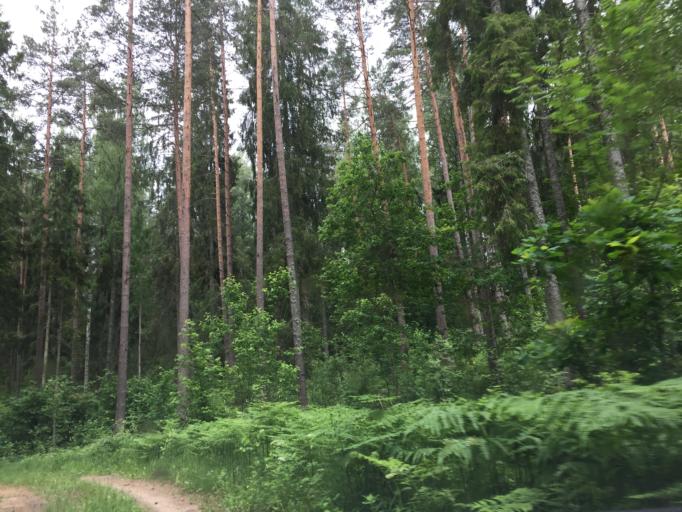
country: LV
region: Tukuma Rajons
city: Tukums
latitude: 57.0298
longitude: 23.0754
